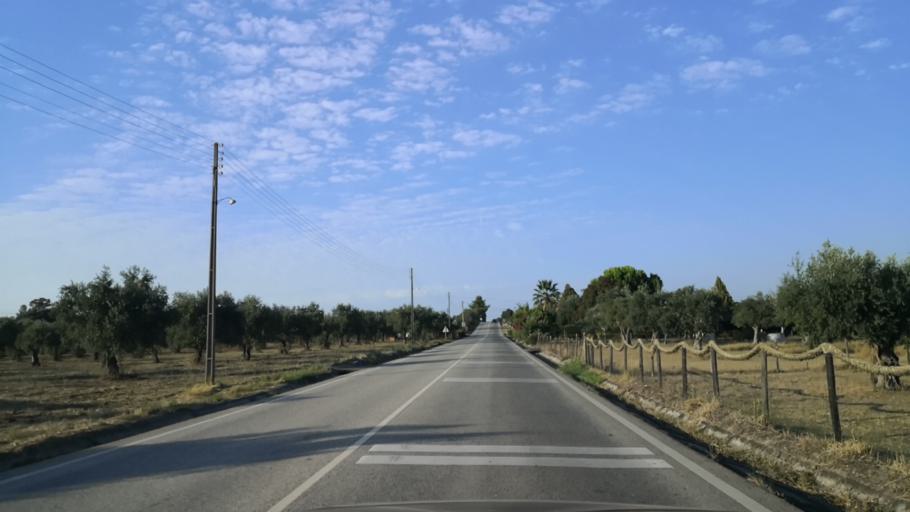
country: PT
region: Santarem
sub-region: Alcanena
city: Alcanena
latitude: 39.3900
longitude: -8.6492
